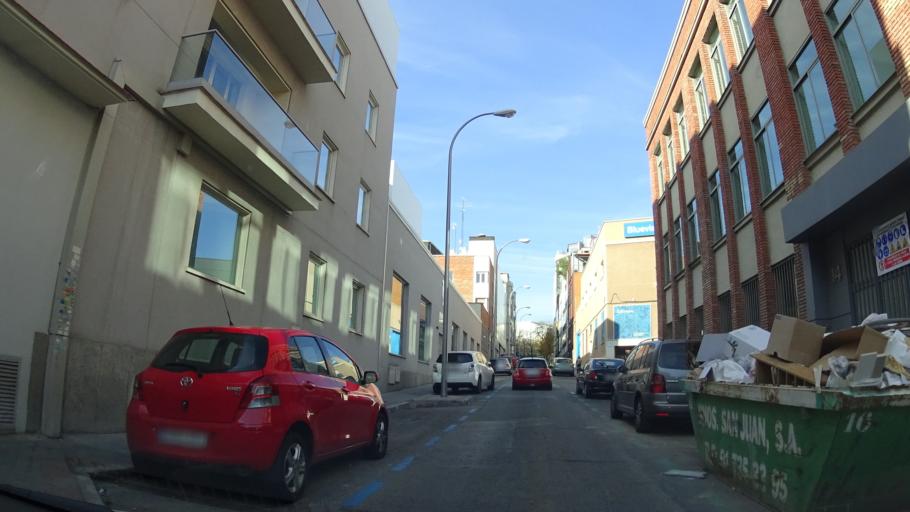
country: ES
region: Madrid
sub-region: Provincia de Madrid
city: Chamartin
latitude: 40.4479
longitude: -3.6712
